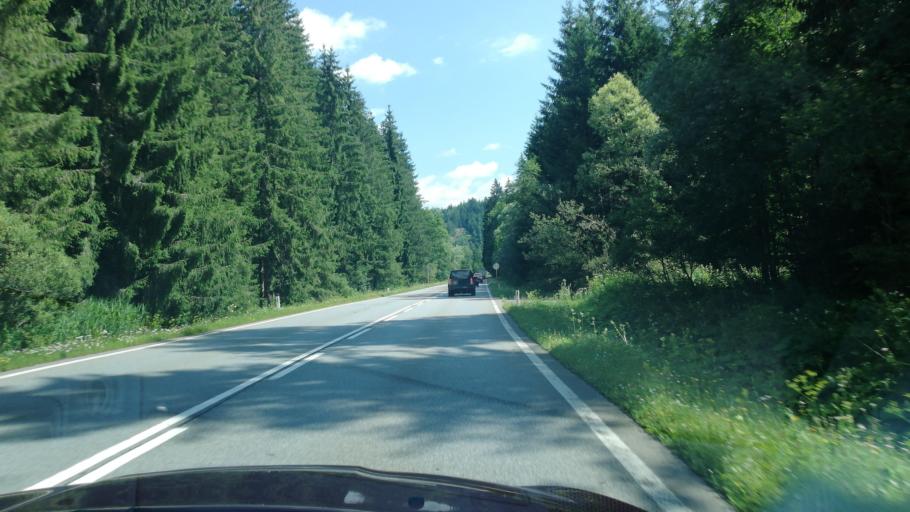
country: AT
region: Styria
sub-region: Politischer Bezirk Murau
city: Sankt Marein bei Neumarkt
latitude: 47.0346
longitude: 14.4188
